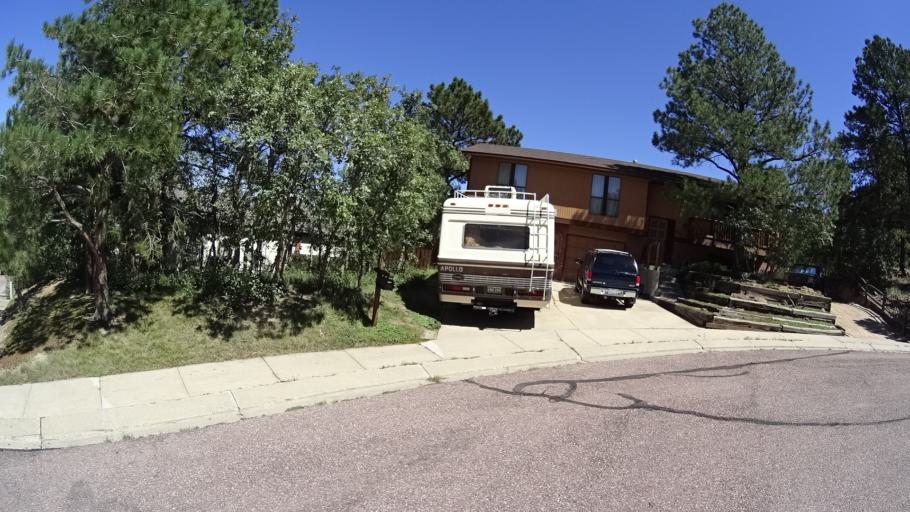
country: US
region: Colorado
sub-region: El Paso County
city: Colorado Springs
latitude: 38.9233
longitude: -104.8073
